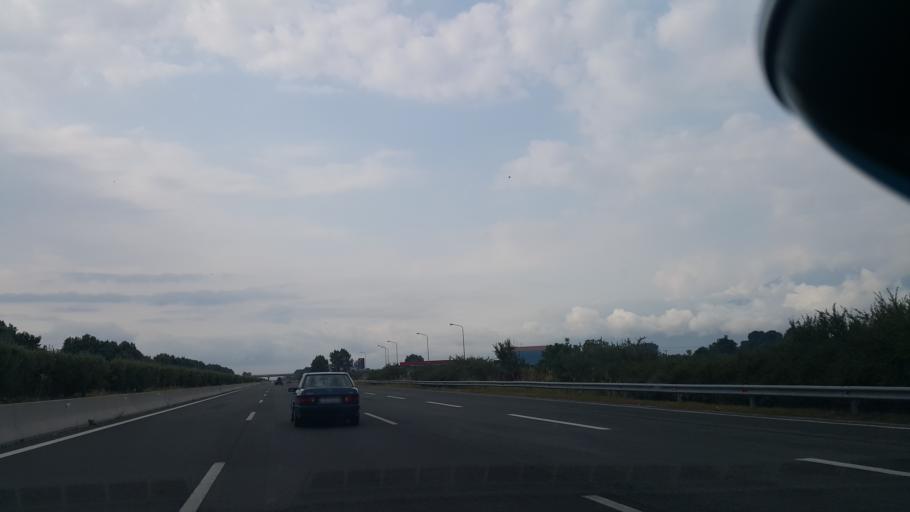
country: GR
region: Central Macedonia
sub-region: Nomos Pierias
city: Nea Efesos
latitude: 40.2338
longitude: 22.5378
